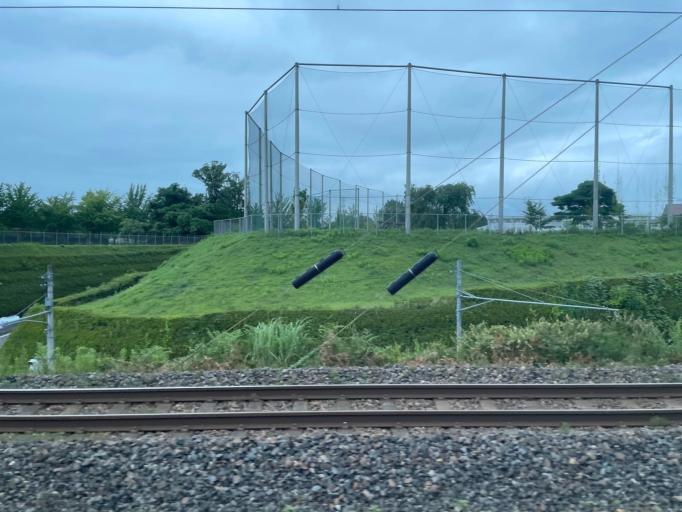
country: JP
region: Tochigi
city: Kuroiso
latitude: 37.0202
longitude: 140.1130
